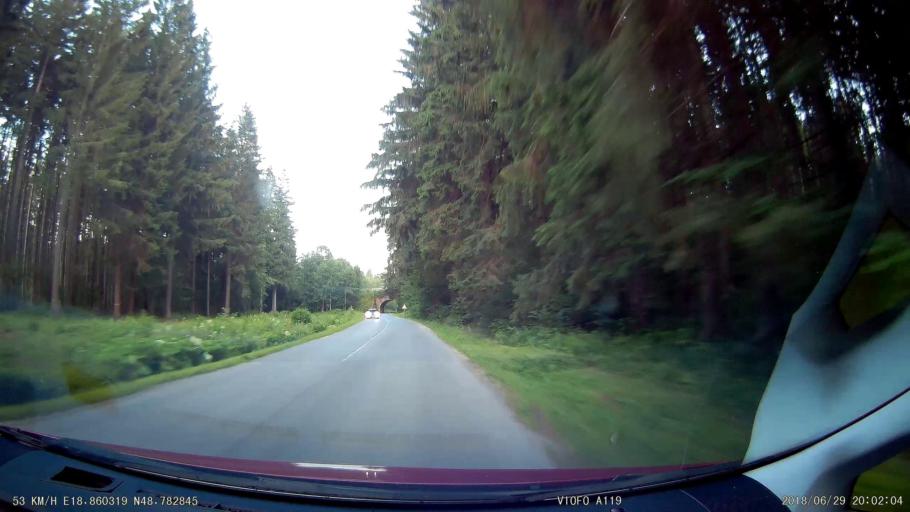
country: SK
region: Banskobystricky
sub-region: Okres Ziar nad Hronom
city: Kremnica
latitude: 48.7828
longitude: 18.8605
